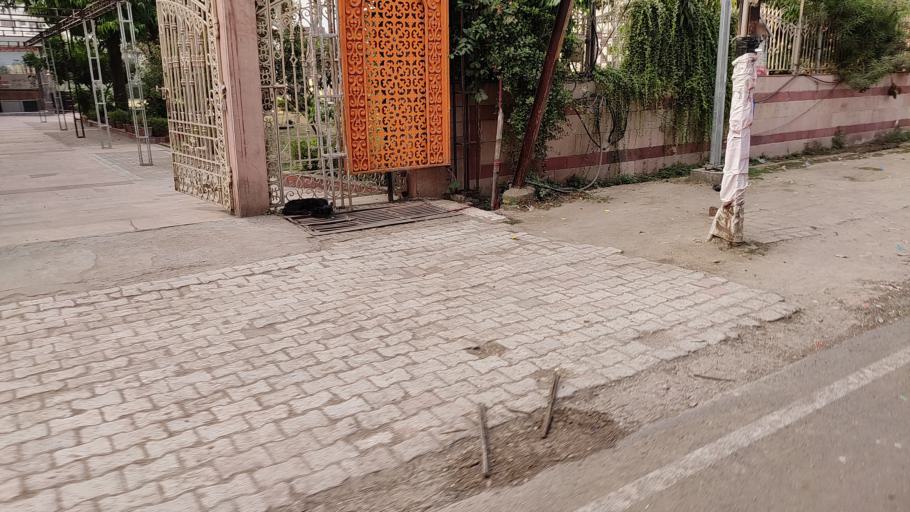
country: IN
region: Uttar Pradesh
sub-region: Mathura
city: Mathura
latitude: 27.5136
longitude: 77.6737
